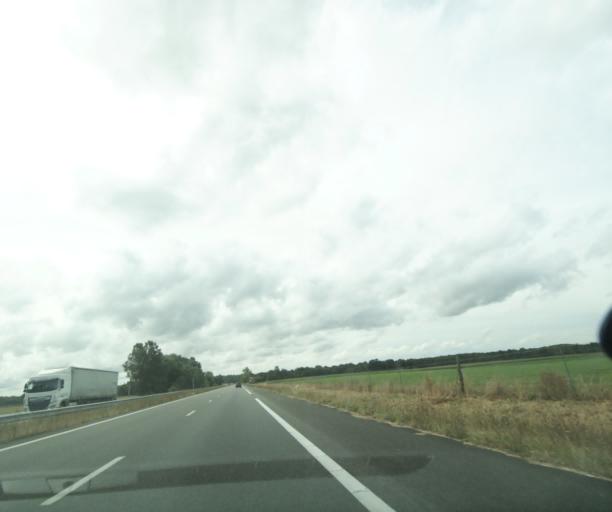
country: FR
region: Poitou-Charentes
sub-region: Departement de la Charente-Maritime
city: Saint-Genis-de-Saintonge
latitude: 45.4852
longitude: -0.6169
